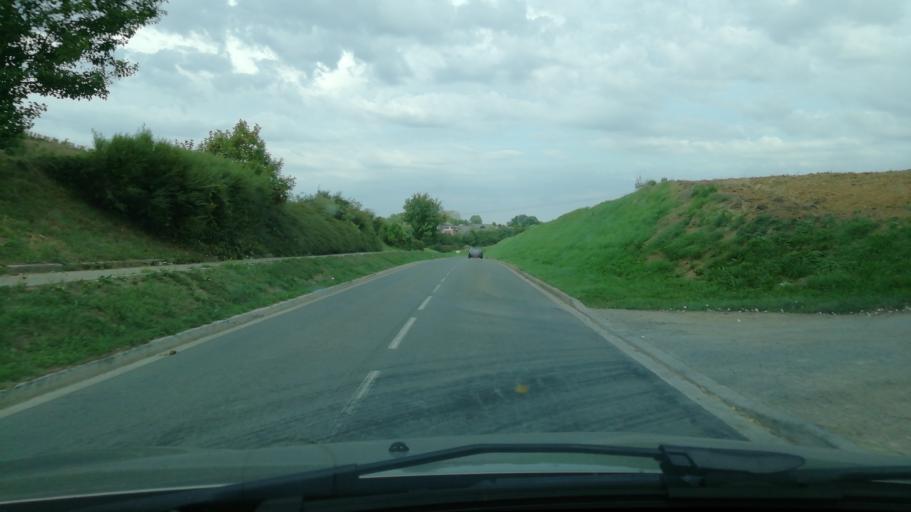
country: FR
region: Nord-Pas-de-Calais
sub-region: Departement du Nord
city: Beauvois-en-Cambresis
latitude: 50.1647
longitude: 3.3573
